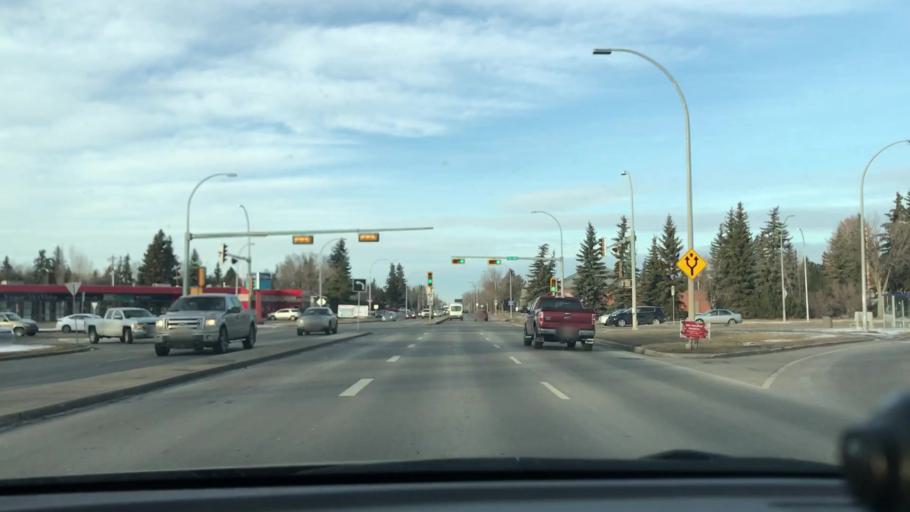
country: CA
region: Alberta
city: Edmonton
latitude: 53.5247
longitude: -113.4429
